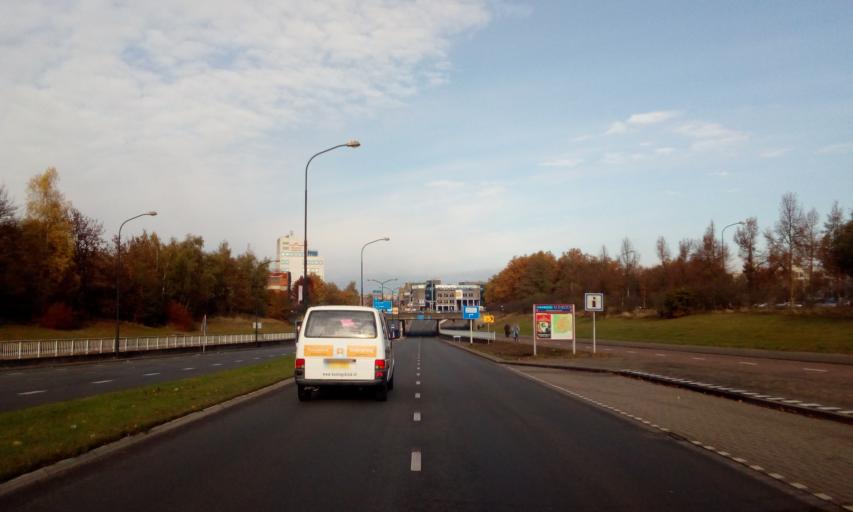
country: NL
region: Gelderland
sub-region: Gemeente Apeldoorn
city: Apeldoorn
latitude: 52.2061
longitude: 5.9584
